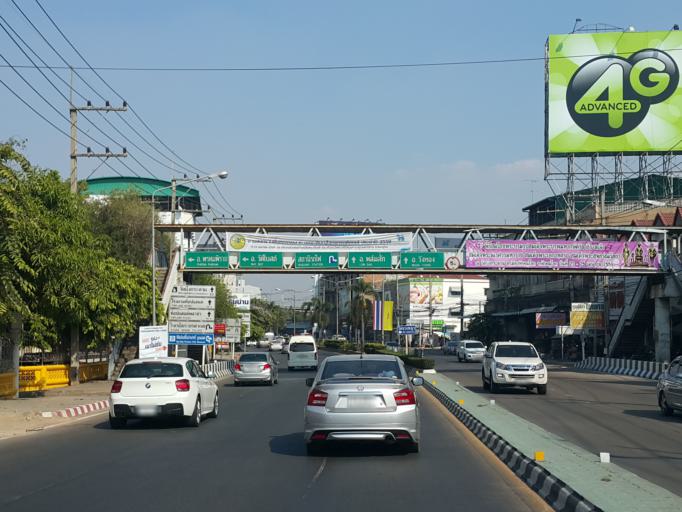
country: TH
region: Phitsanulok
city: Phitsanulok
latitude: 16.8222
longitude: 100.2614
